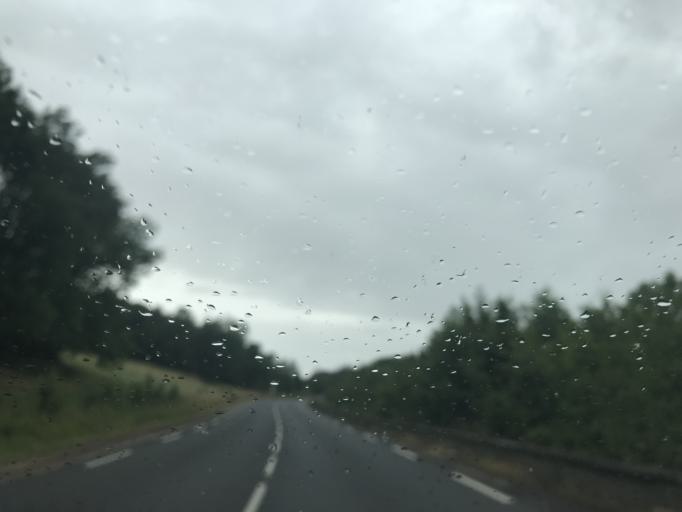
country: FR
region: Auvergne
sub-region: Departement de la Haute-Loire
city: Polignac
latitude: 45.0629
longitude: 3.8587
